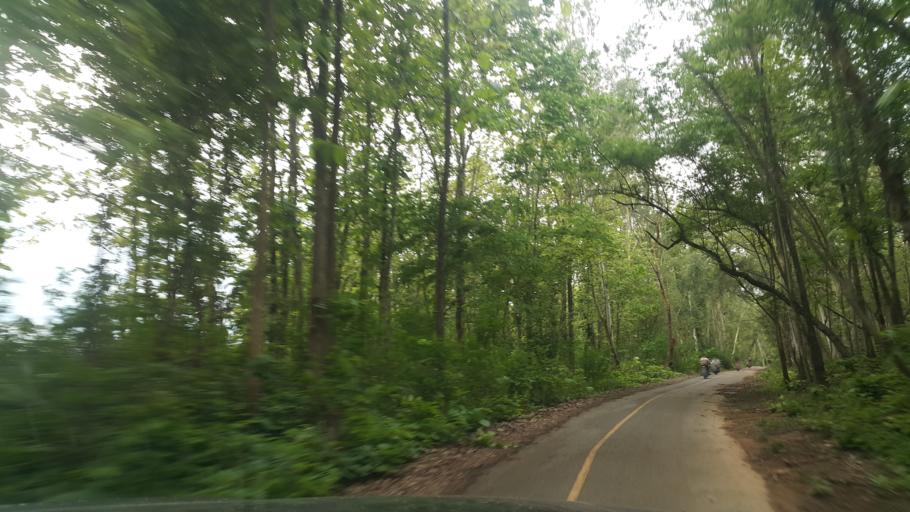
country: TH
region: Chiang Mai
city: Mae On
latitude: 18.7195
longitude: 99.2333
